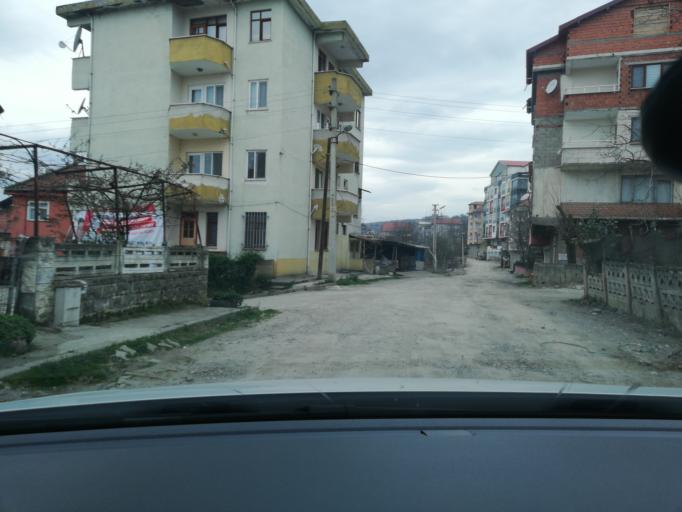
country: TR
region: Zonguldak
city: Gokcebey
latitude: 41.3089
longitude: 32.1370
